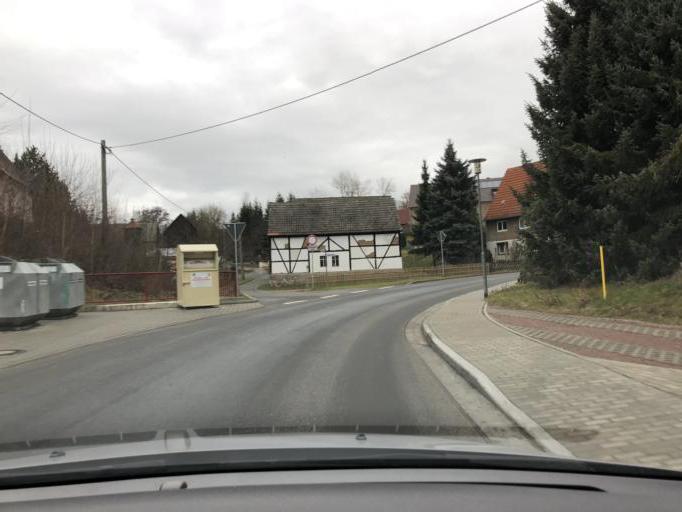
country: DE
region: Saxony
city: Rosswein
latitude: 51.0742
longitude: 13.2372
